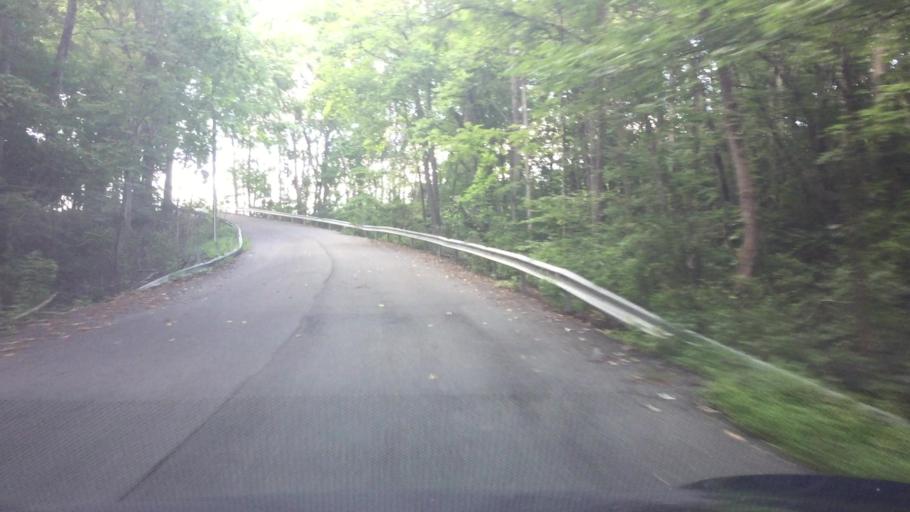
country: US
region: Virginia
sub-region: Wythe County
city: Wytheville
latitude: 36.9456
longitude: -81.0515
